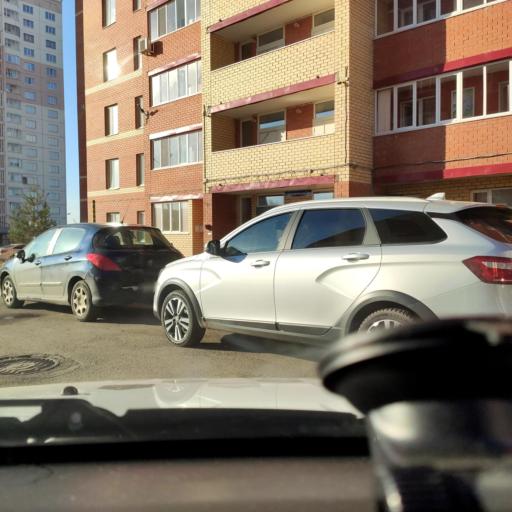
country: RU
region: Perm
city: Perm
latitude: 57.9851
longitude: 56.2827
